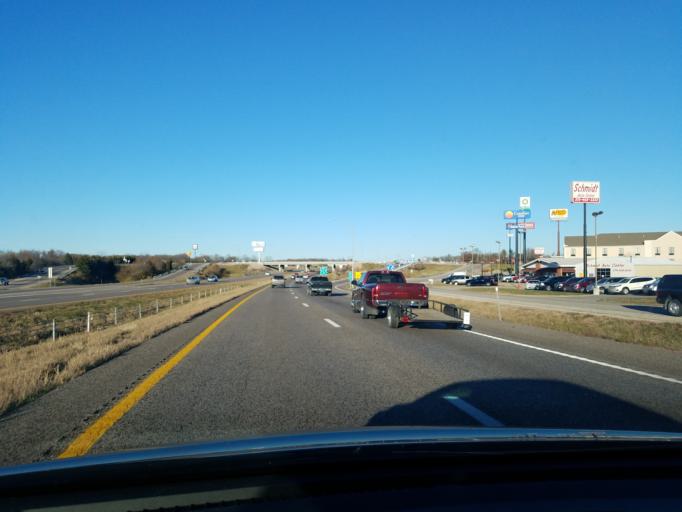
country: US
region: Missouri
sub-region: Franklin County
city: Sullivan
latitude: 38.2091
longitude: -91.1743
